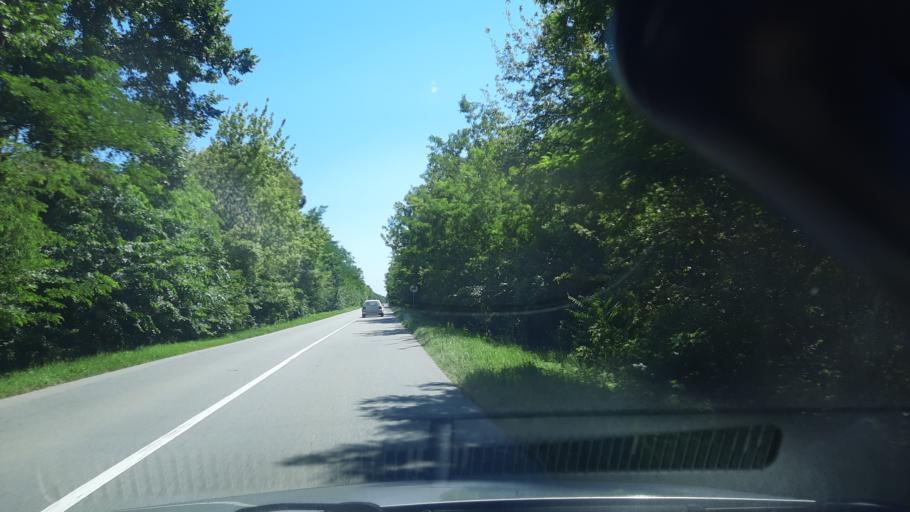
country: RO
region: Caras-Severin
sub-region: Comuna Socol
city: Socol
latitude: 44.8091
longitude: 21.2283
